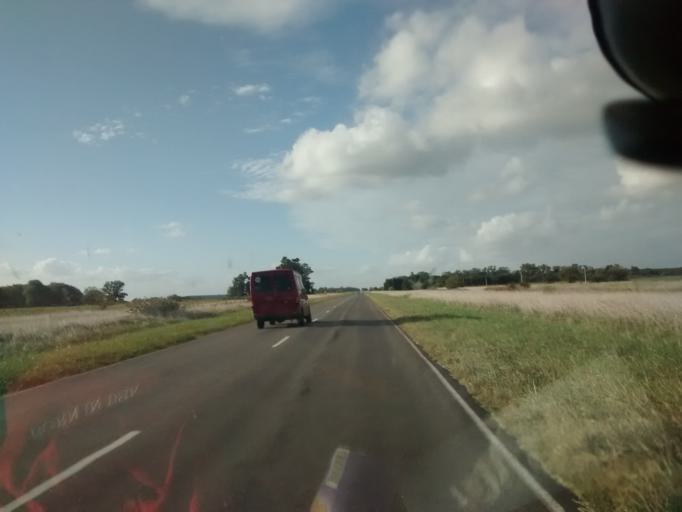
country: AR
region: Buenos Aires
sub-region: Partido de Ayacucho
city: Ayacucho
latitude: -36.6543
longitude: -58.5738
